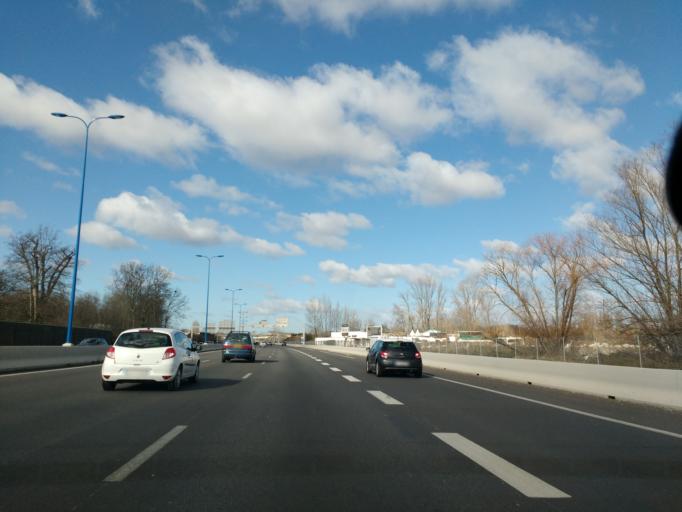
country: FR
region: Midi-Pyrenees
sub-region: Departement de la Haute-Garonne
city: Ramonville-Saint-Agne
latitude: 43.5671
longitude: 1.4825
